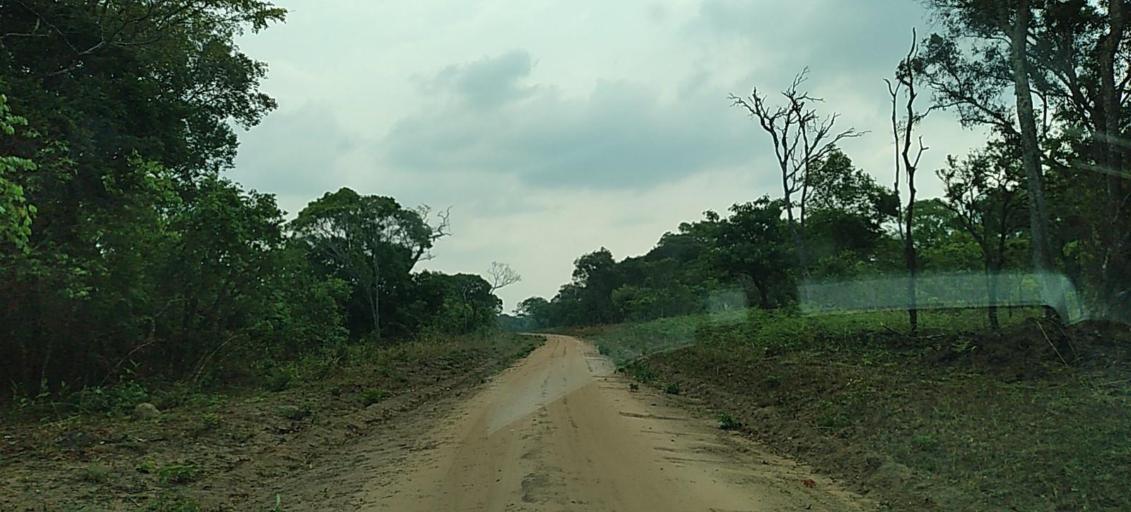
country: ZM
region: North-Western
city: Mwinilunga
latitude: -11.4122
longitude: 24.6161
